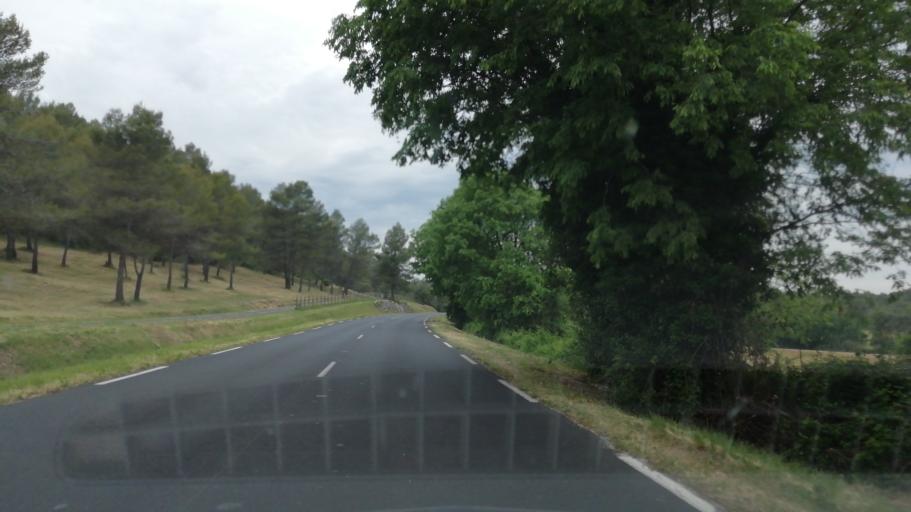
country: FR
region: Languedoc-Roussillon
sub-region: Departement de l'Herault
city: Prades-le-Lez
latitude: 43.7037
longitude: 3.8486
